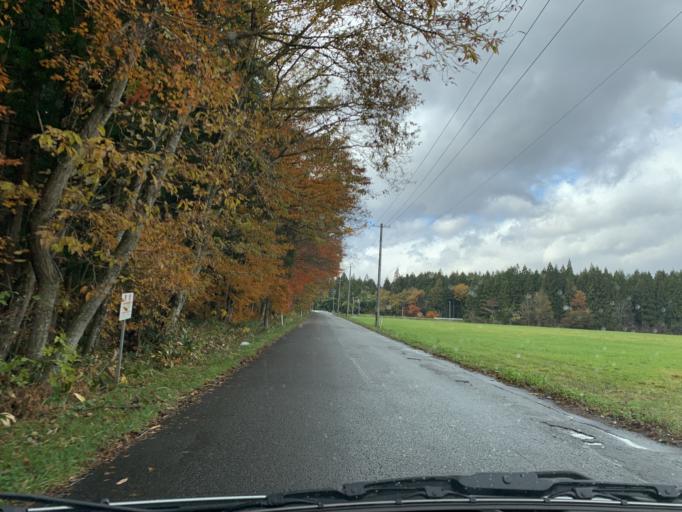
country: JP
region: Iwate
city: Mizusawa
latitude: 39.1038
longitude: 140.9899
